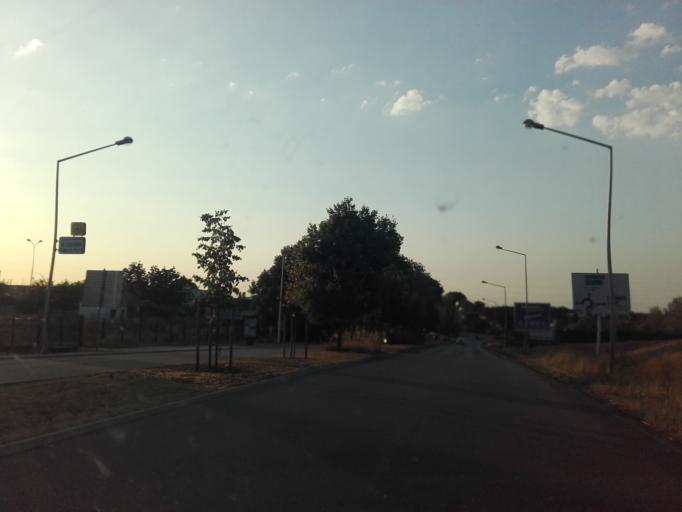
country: FR
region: Bourgogne
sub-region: Departement de l'Yonne
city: Auxerre
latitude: 47.8138
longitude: 3.5617
